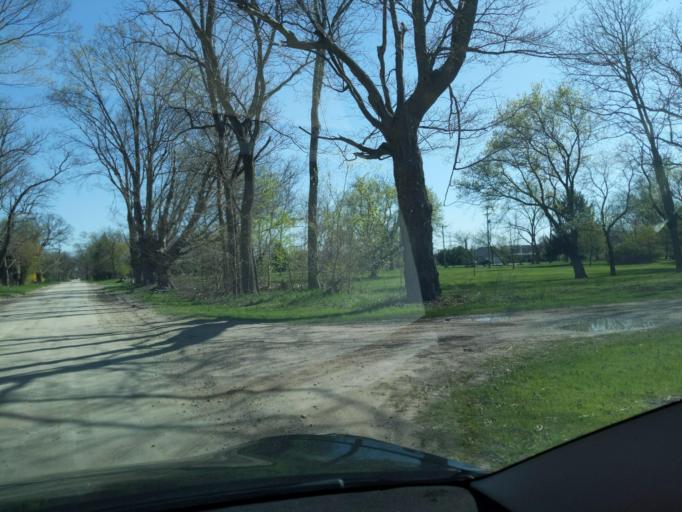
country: US
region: Michigan
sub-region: Ingham County
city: Stockbridge
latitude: 42.4150
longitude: -84.0836
